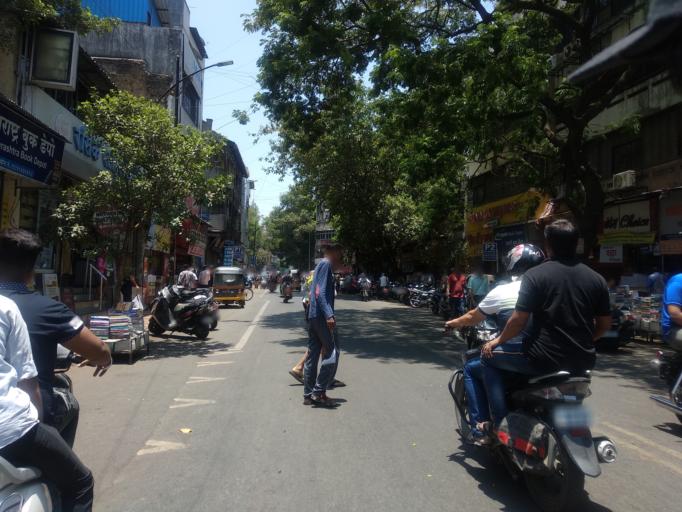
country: IN
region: Maharashtra
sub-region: Pune Division
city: Pune
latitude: 18.5166
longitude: 73.8540
